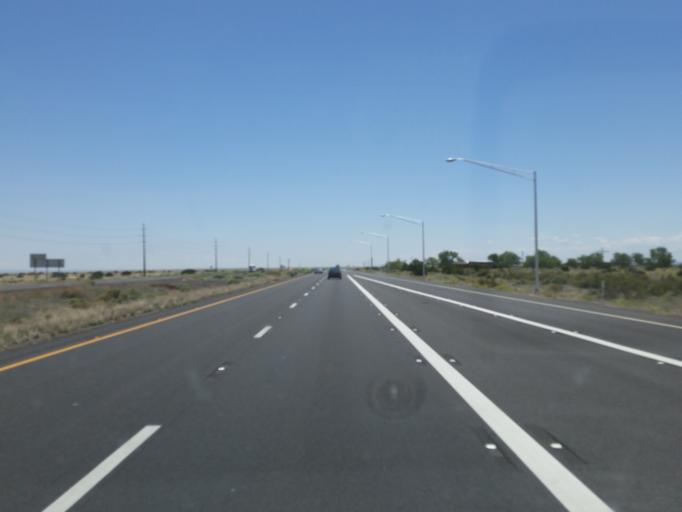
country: US
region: Arizona
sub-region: Coconino County
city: Flagstaff
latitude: 35.1597
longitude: -111.2679
